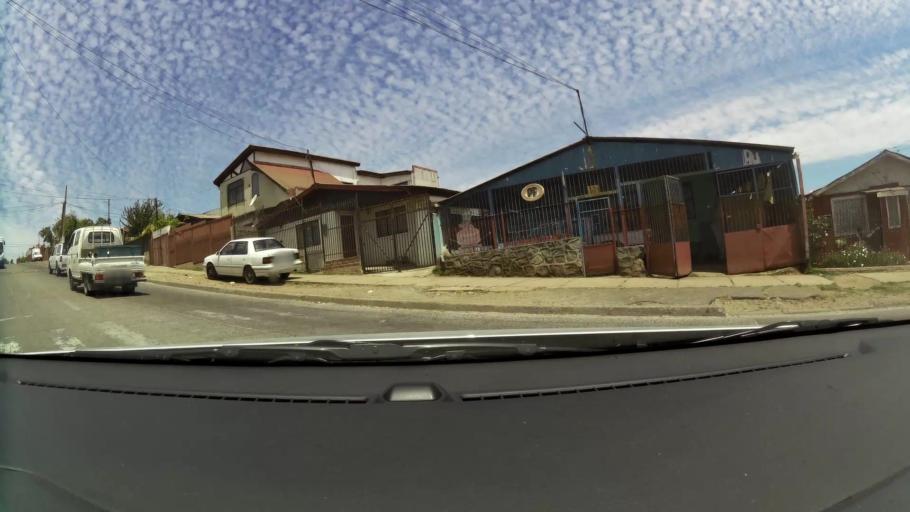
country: CL
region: Valparaiso
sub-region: Provincia de Valparaiso
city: Vina del Mar
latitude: -33.0534
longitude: -71.5647
